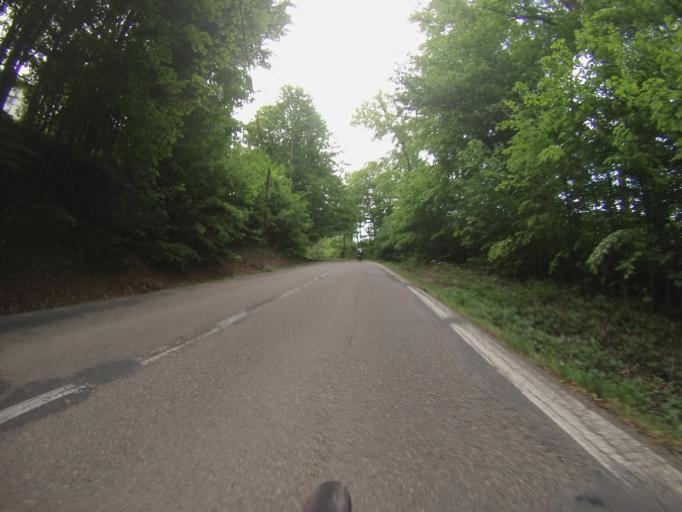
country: CZ
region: South Moravian
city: Veverska Bityska
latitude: 49.2497
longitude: 16.4863
